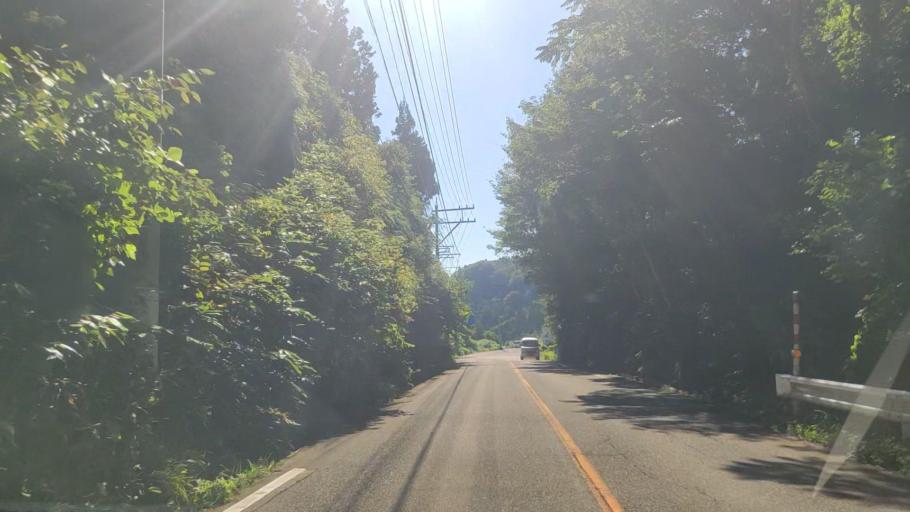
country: JP
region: Ishikawa
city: Nanao
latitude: 37.3154
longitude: 137.1579
